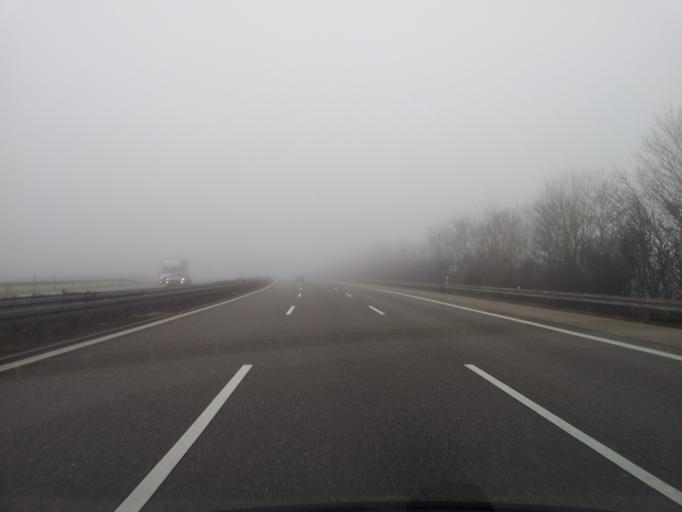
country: DE
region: Baden-Wuerttemberg
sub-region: Freiburg Region
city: Engen
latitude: 47.8912
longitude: 8.7525
